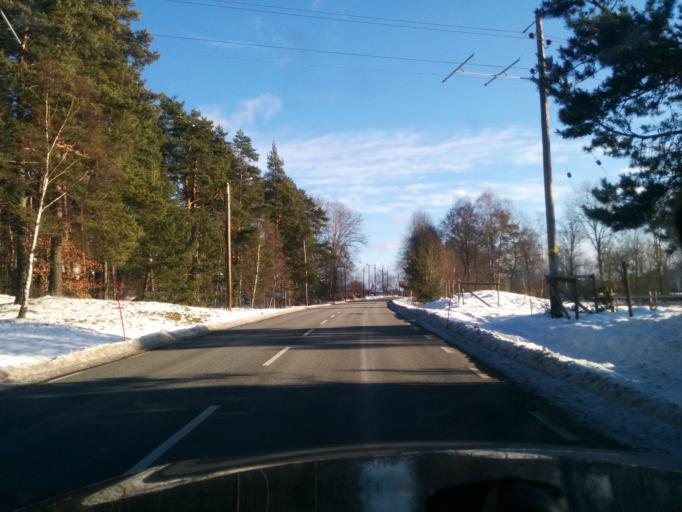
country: SE
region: Stockholm
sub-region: Taby Kommun
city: Taby
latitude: 59.4897
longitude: 18.0666
